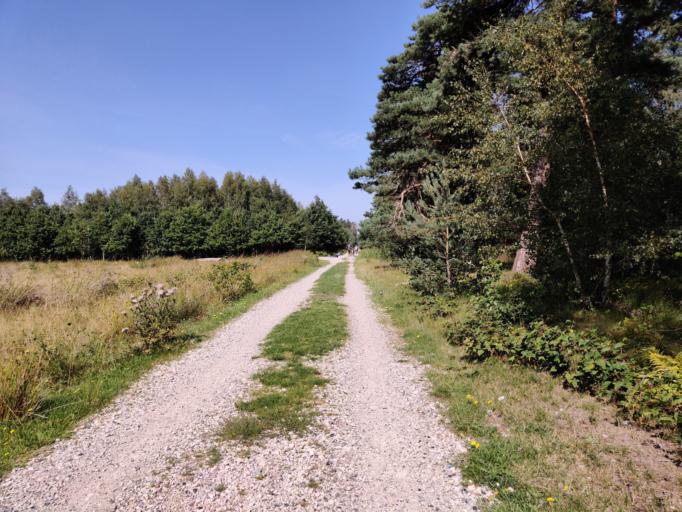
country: DK
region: Zealand
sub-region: Guldborgsund Kommune
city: Nykobing Falster
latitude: 54.6237
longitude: 11.9569
